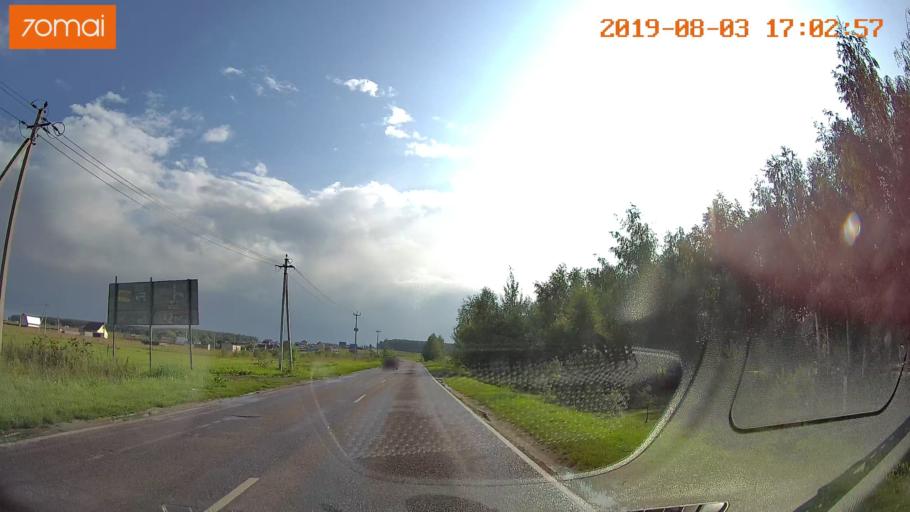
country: RU
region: Moskovskaya
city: Troitskoye
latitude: 55.3423
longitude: 38.5795
